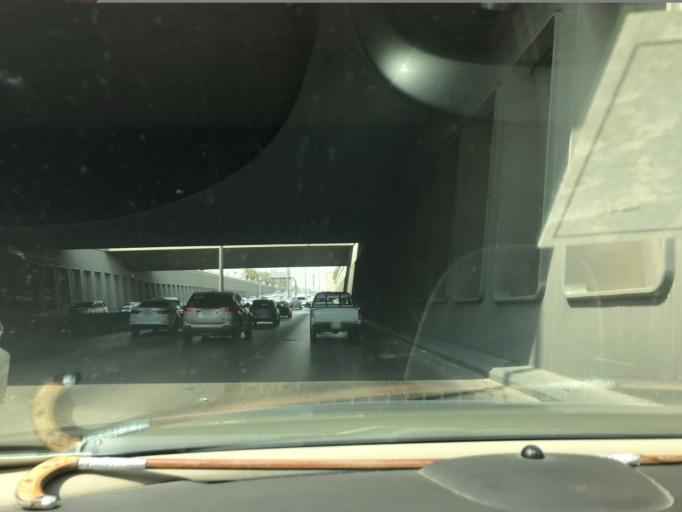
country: SA
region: Ar Riyad
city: Riyadh
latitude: 24.6682
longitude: 46.6960
